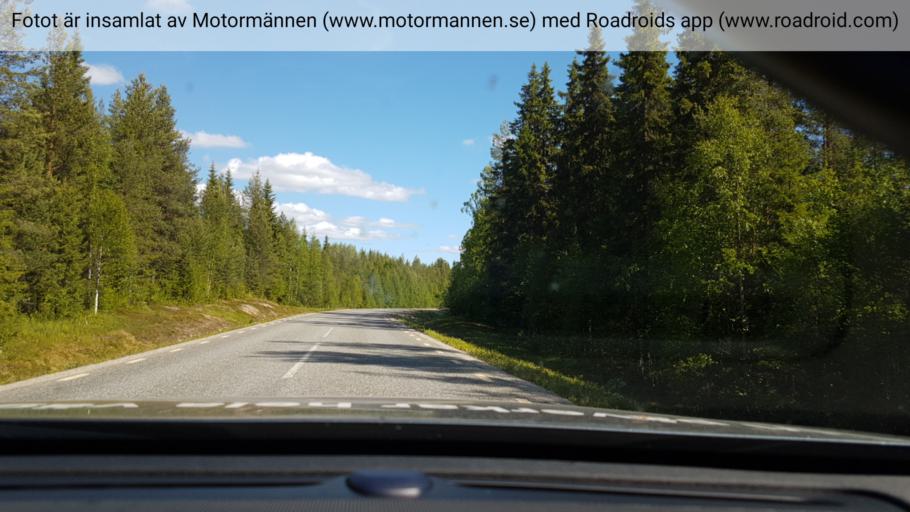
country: SE
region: Vaesterbotten
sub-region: Lycksele Kommun
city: Lycksele
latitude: 64.6123
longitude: 18.4880
